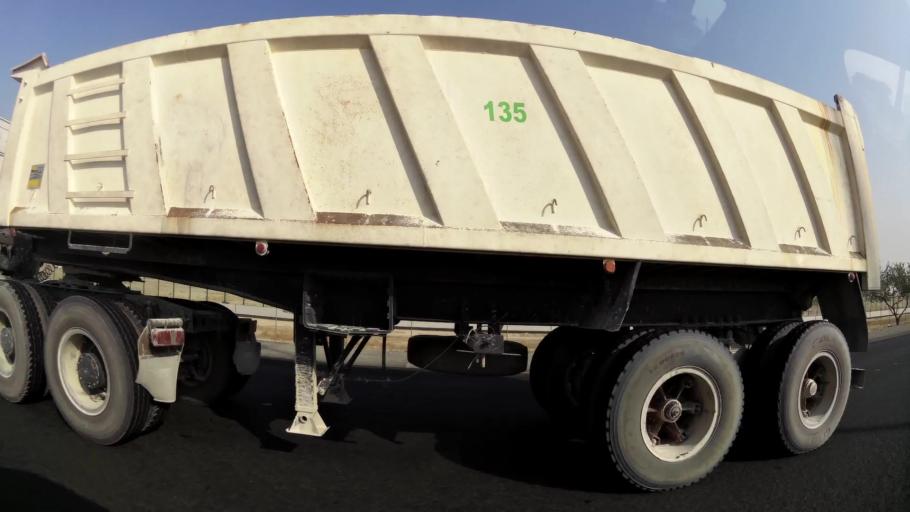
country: KW
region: Al Farwaniyah
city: Janub as Surrah
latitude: 29.1829
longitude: 47.9355
